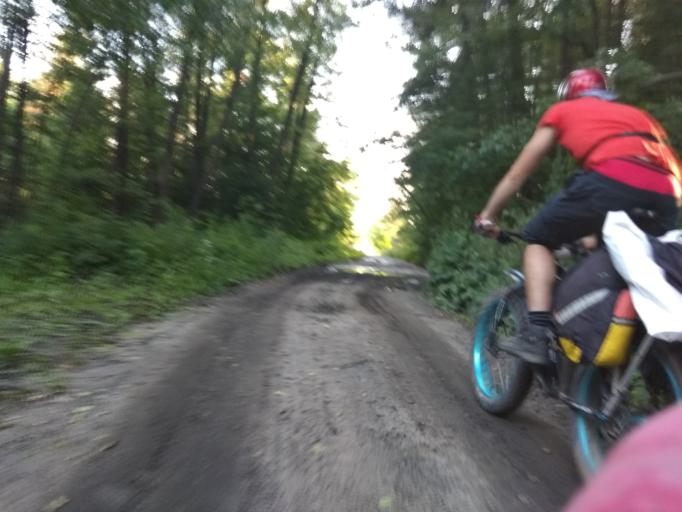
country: RU
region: Moskovskaya
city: Misheronskiy
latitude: 55.7238
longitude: 39.7484
